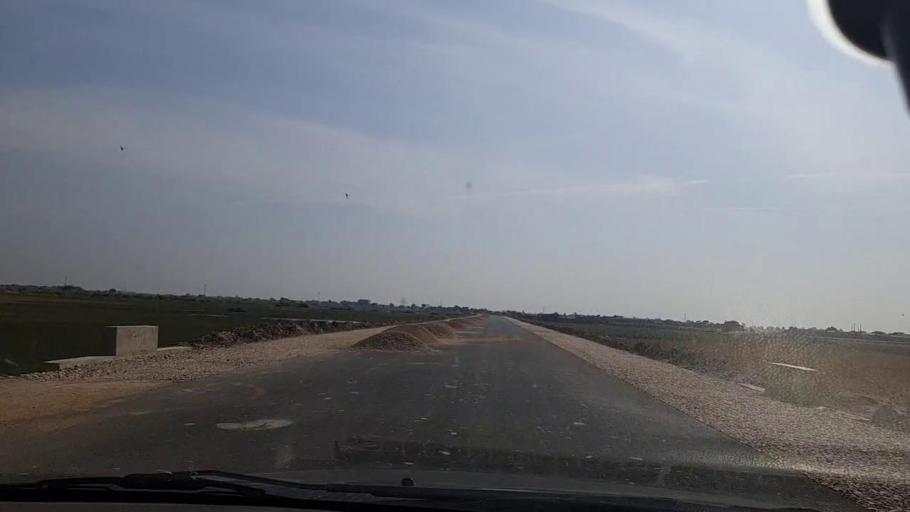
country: PK
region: Sindh
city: Mirpur Batoro
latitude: 24.7480
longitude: 68.2714
